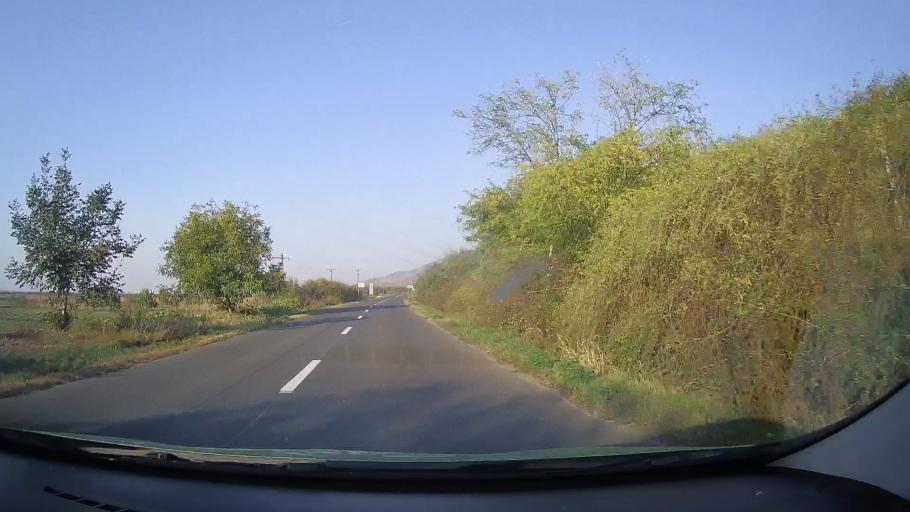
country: RO
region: Arad
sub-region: Comuna Covasint
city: Covasint
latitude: 46.2112
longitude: 21.6119
